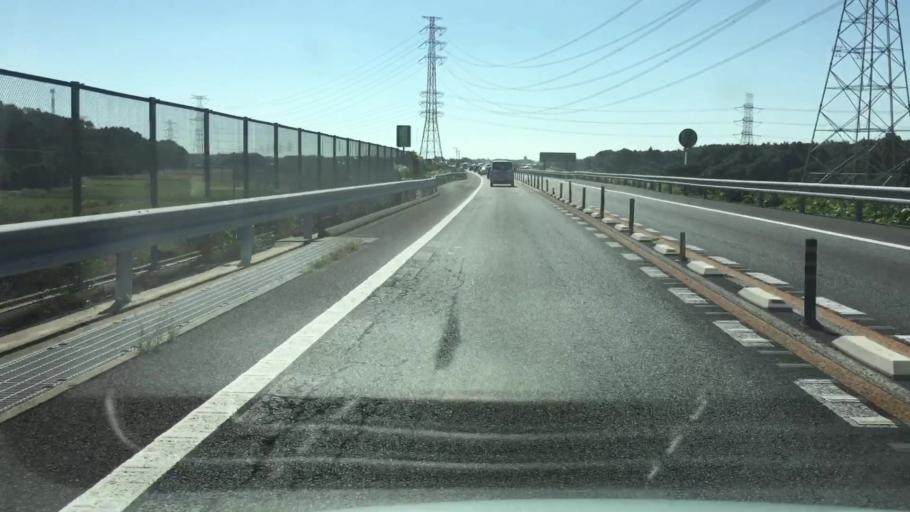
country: JP
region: Ibaraki
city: Ushiku
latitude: 36.0062
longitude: 140.1448
